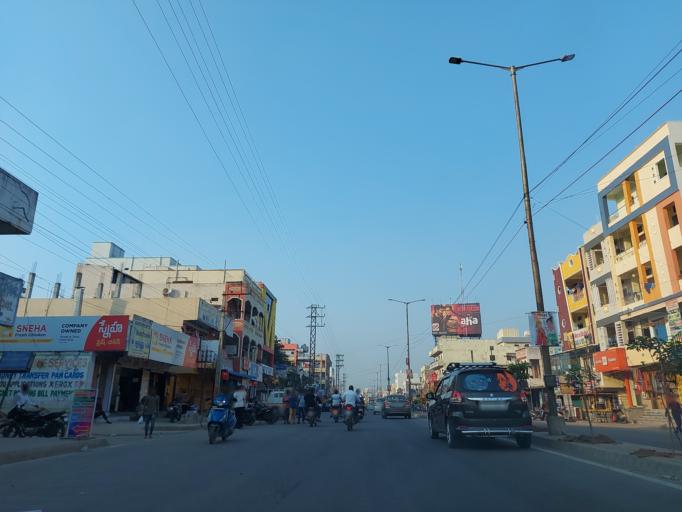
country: IN
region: Telangana
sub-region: Rangareddi
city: Balapur
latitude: 17.2075
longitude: 78.4765
